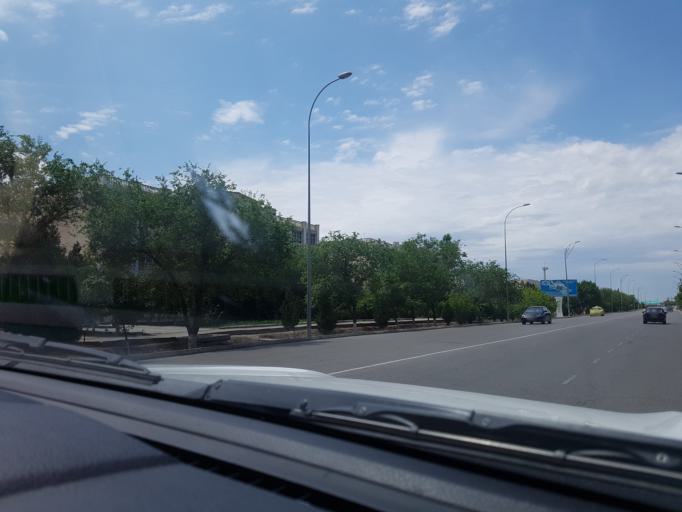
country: TM
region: Dasoguz
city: Dasoguz
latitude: 41.8433
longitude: 59.9365
